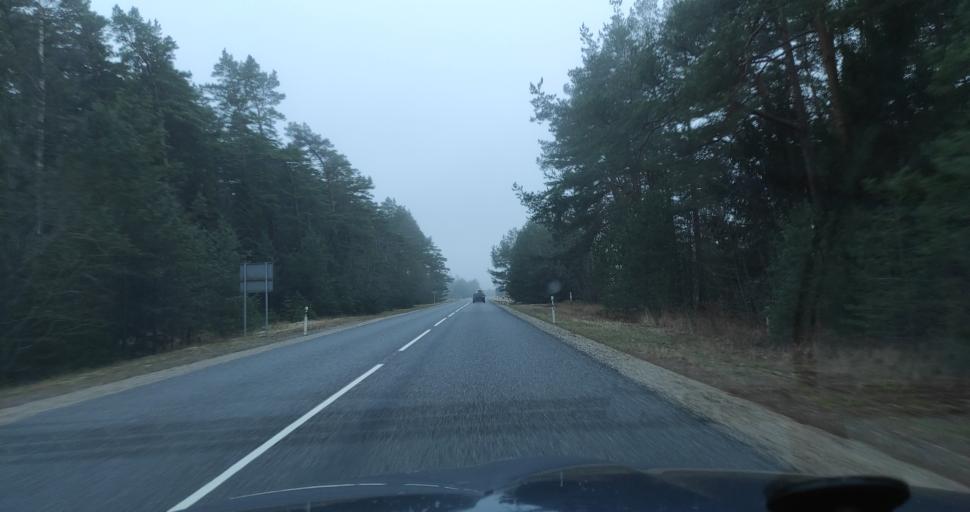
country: LV
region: Pavilostas
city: Pavilosta
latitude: 56.9670
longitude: 21.3401
